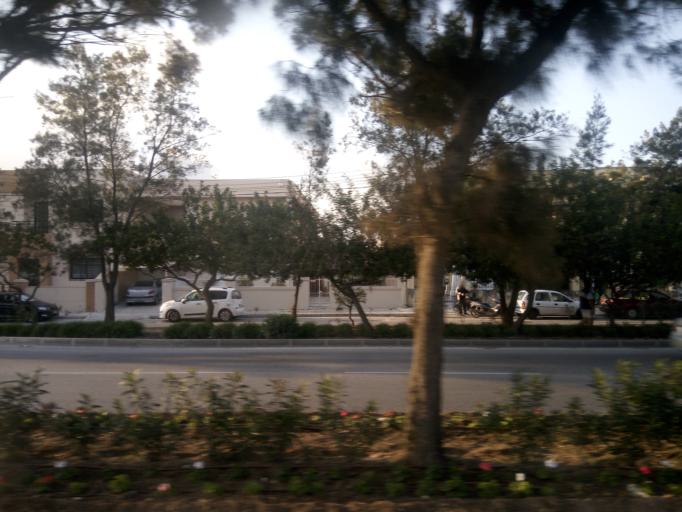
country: MT
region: Balzan
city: Balzan
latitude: 35.8932
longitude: 14.4519
